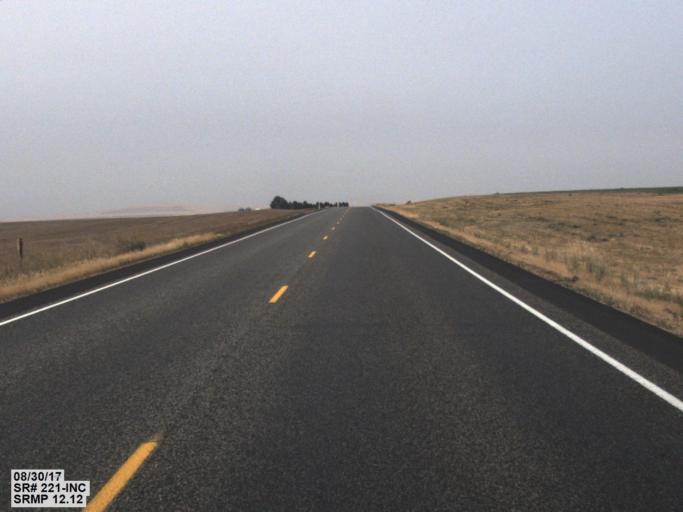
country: US
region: Washington
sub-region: Benton County
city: Benton City
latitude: 46.1107
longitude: -119.6018
